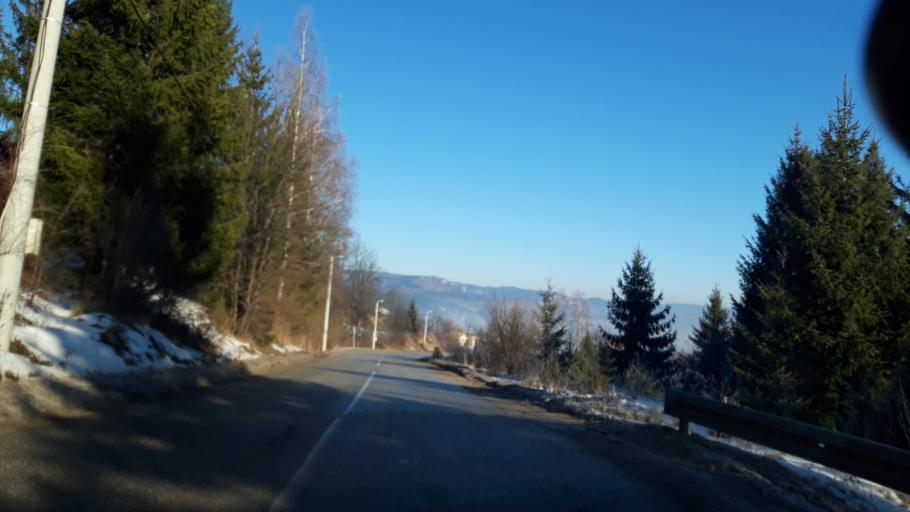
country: BA
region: Republika Srpska
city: Koran
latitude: 43.8058
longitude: 18.5536
